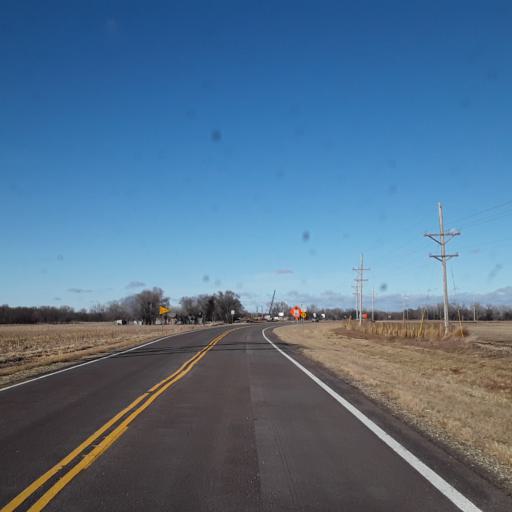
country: US
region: Kansas
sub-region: Cloud County
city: Concordia
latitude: 39.5699
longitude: -97.7063
